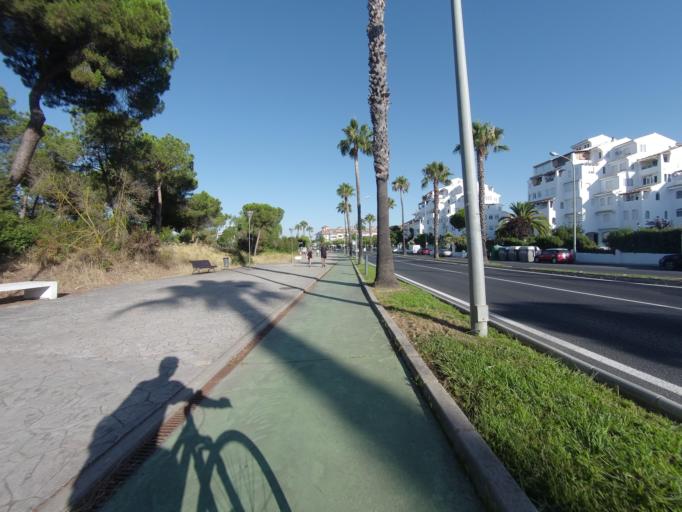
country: ES
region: Andalusia
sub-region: Provincia de Huelva
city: Aljaraque
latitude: 37.2126
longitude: -7.0610
